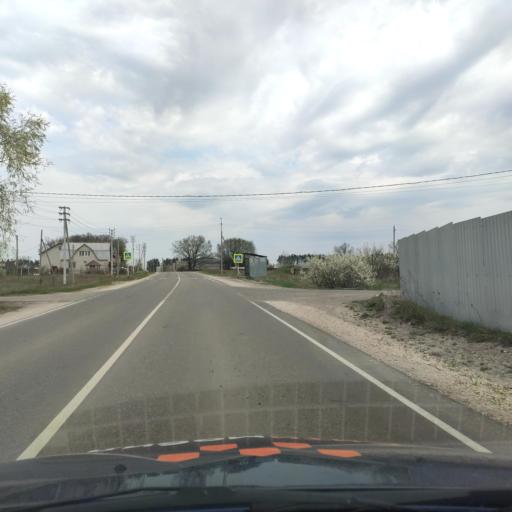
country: RU
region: Voronezj
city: Podgornoye
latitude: 51.8713
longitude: 39.1728
